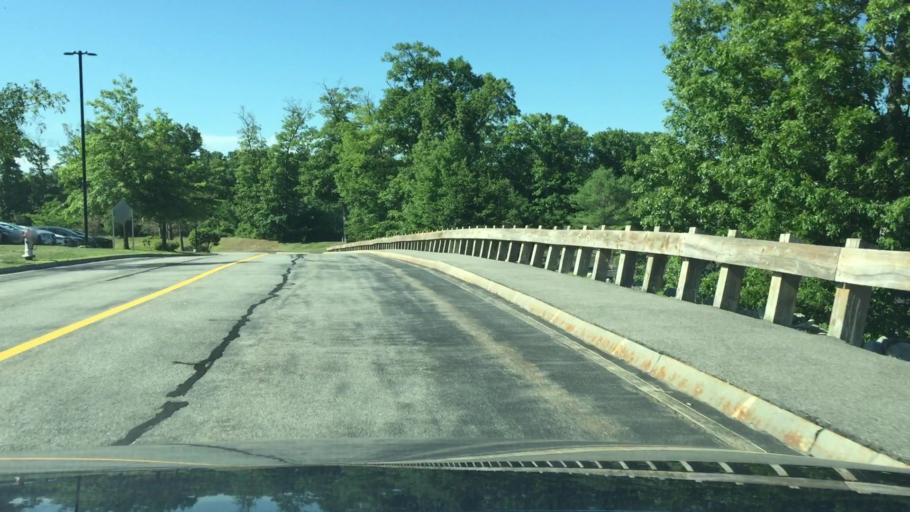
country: US
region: Massachusetts
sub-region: Middlesex County
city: Marlborough
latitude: 42.3243
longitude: -71.5858
